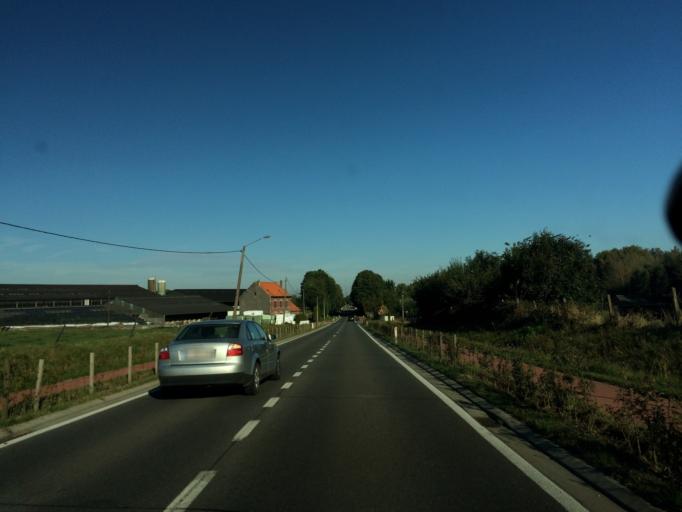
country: BE
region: Flanders
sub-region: Provincie Vlaams-Brabant
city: Merchtem
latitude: 50.9352
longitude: 4.2513
